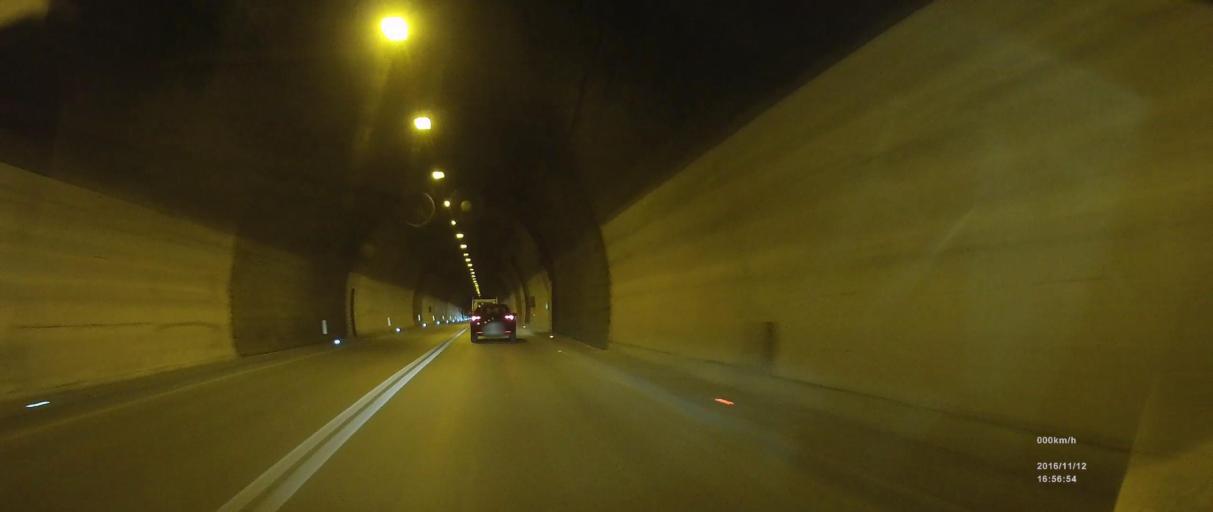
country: HR
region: Splitsko-Dalmatinska
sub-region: Grad Split
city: Split
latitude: 43.5076
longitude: 16.4249
